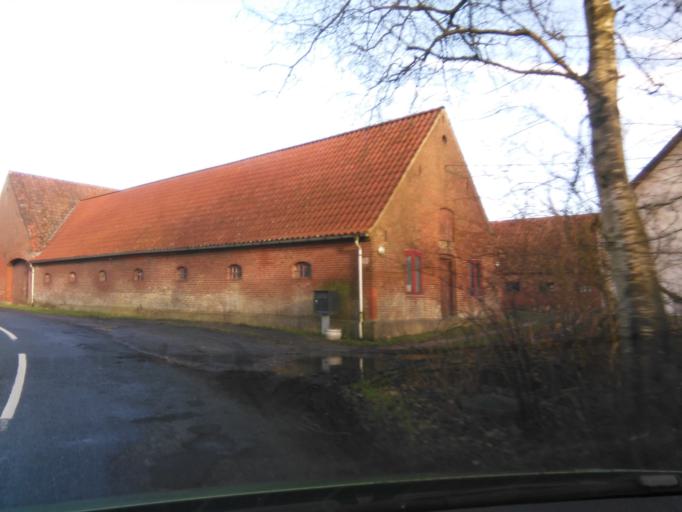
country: DK
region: Central Jutland
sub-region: Arhus Kommune
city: Solbjerg
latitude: 56.0311
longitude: 10.1256
